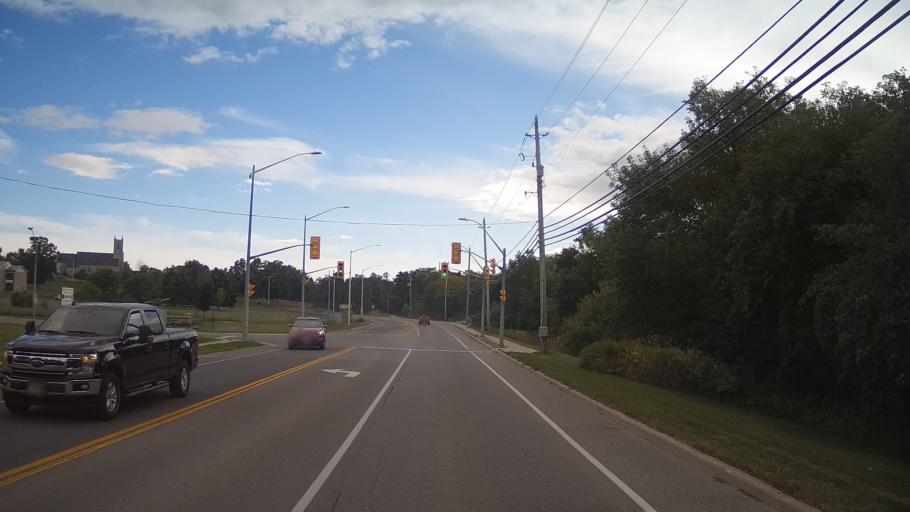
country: CA
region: Ontario
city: Kingston
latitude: 44.2470
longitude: -76.4617
